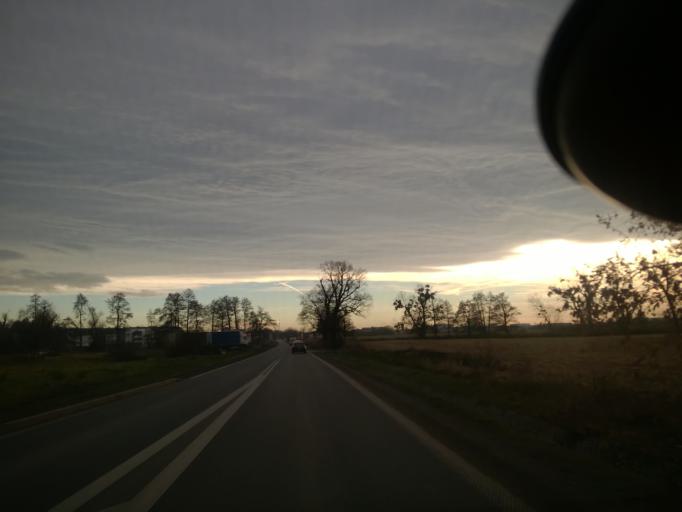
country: PL
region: Lower Silesian Voivodeship
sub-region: Powiat wroclawski
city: Bielany Wroclawskie
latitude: 51.0856
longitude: 16.9538
